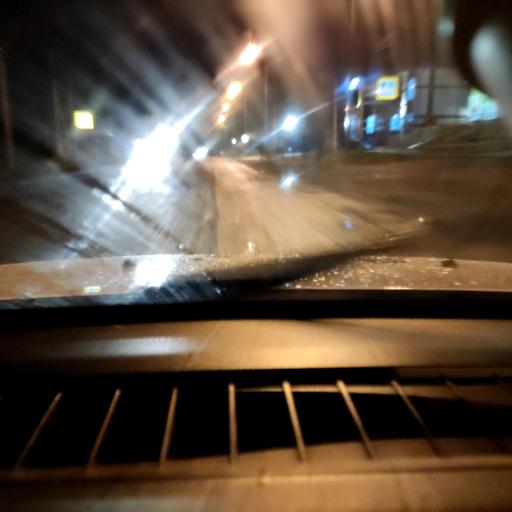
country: RU
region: Udmurtiya
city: Khokhryaki
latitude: 57.1913
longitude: 53.1546
